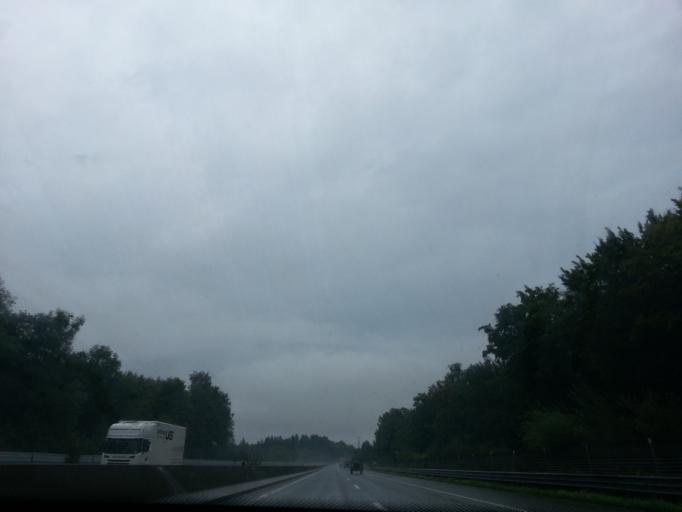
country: AT
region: Upper Austria
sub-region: Politischer Bezirk Vocklabruck
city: Sankt Georgen im Attergau
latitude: 47.9133
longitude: 13.4567
